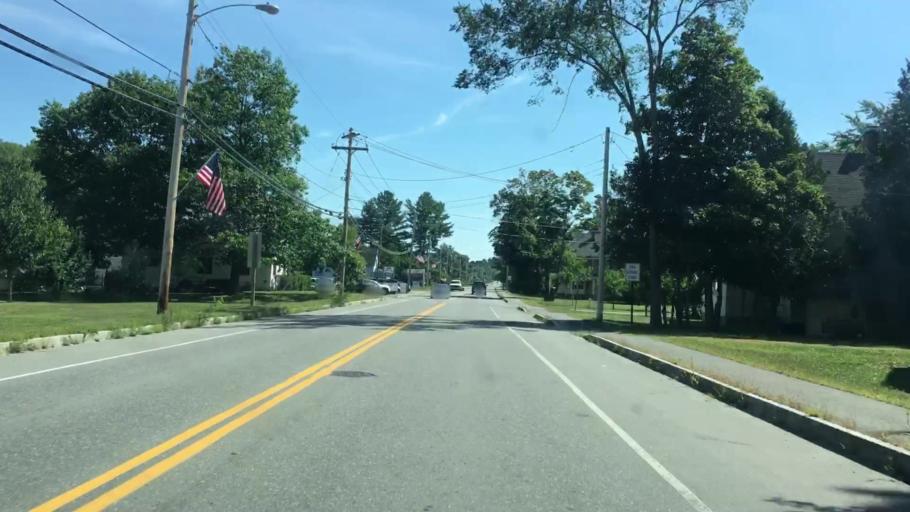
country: US
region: Maine
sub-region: Piscataquis County
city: Milo
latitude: 45.2493
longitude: -68.9808
